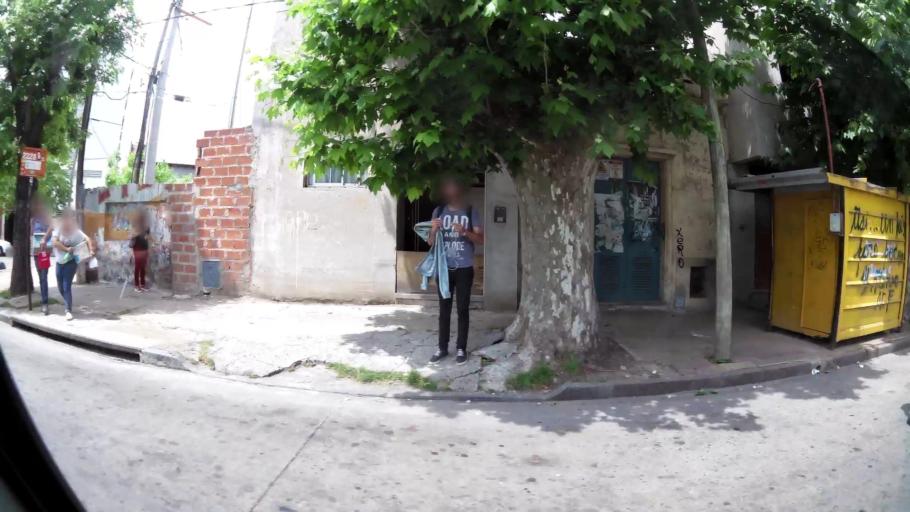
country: AR
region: Buenos Aires
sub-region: Partido de La Plata
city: La Plata
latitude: -34.9450
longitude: -57.9531
